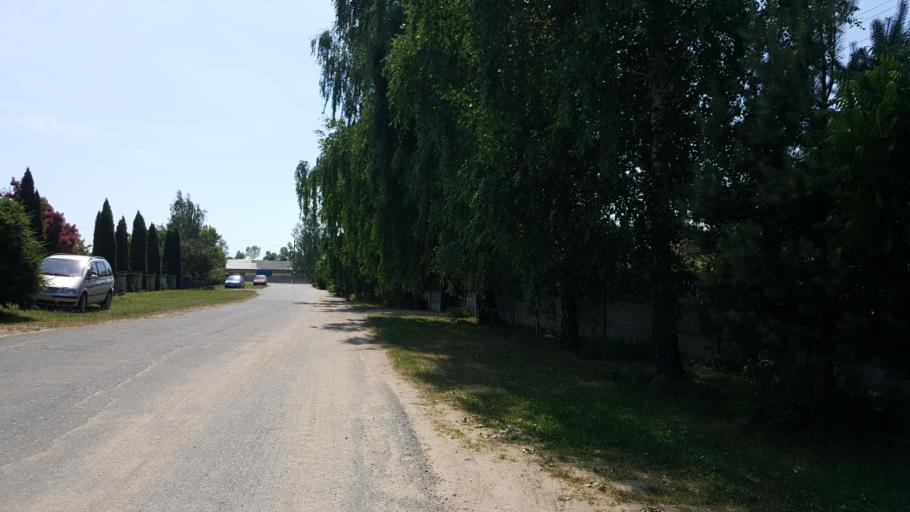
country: BY
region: Brest
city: Kamyanyets
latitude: 52.3977
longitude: 23.8354
